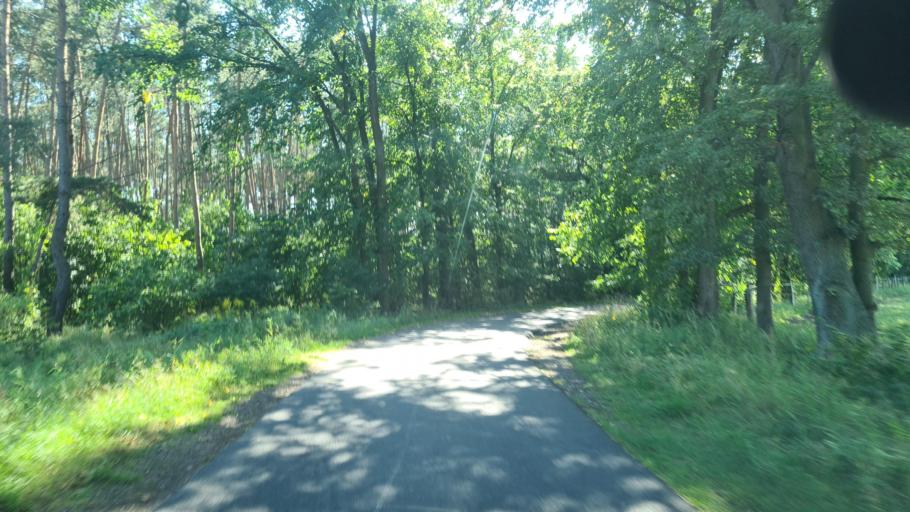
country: DE
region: Brandenburg
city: Nauen
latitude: 52.6360
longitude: 12.9439
